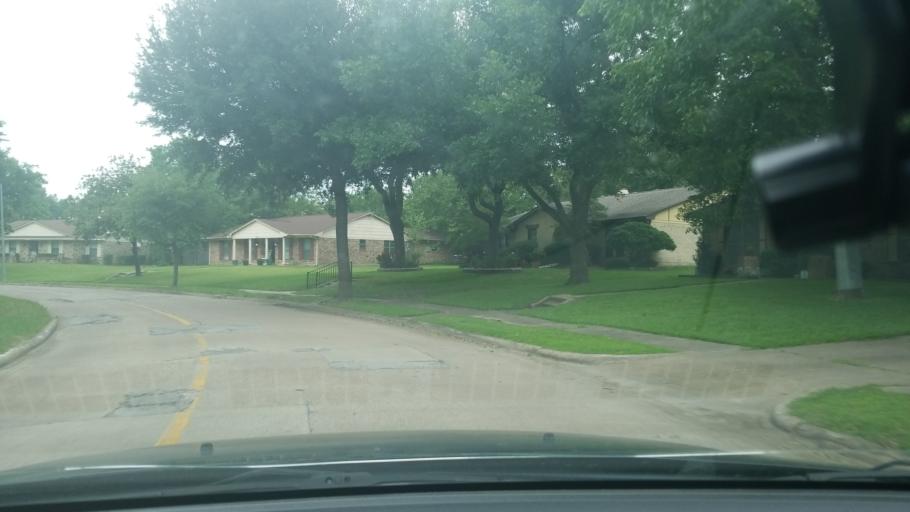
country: US
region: Texas
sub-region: Dallas County
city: Mesquite
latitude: 32.7841
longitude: -96.6335
